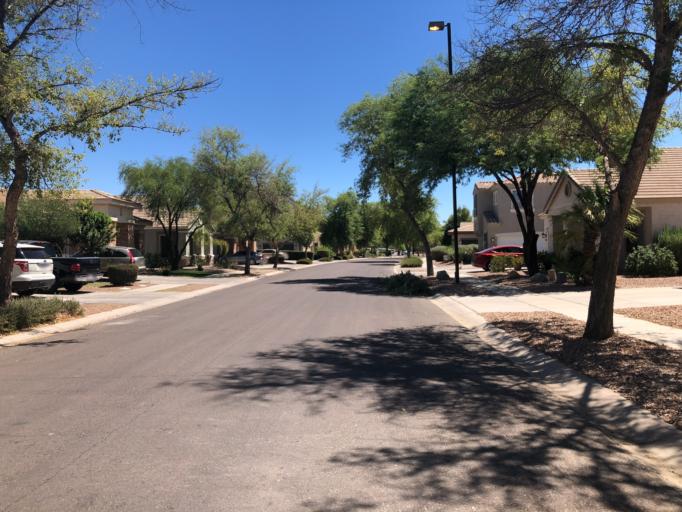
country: US
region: Arizona
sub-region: Maricopa County
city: Queen Creek
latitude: 33.2679
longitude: -111.6988
